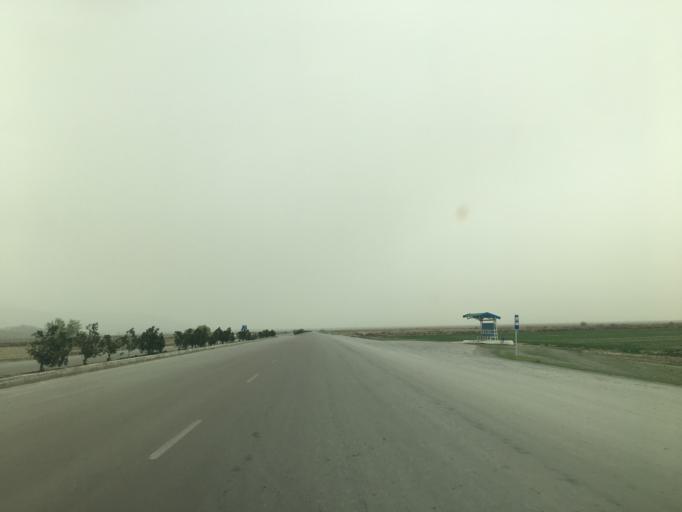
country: TM
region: Ahal
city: Baharly
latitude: 38.3287
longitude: 57.5835
